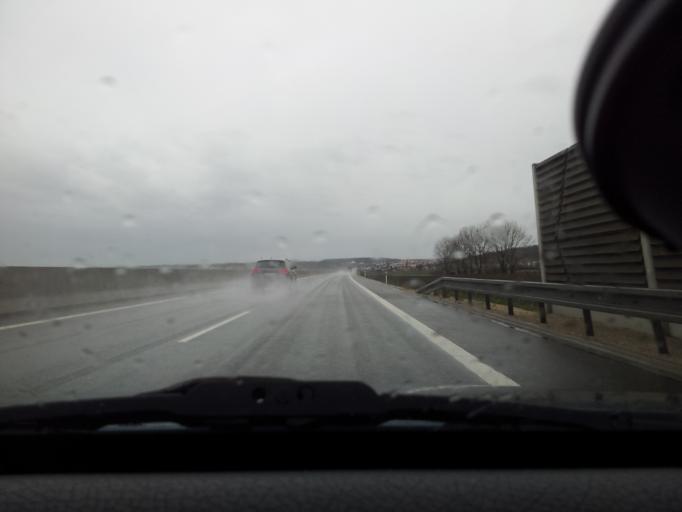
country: SK
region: Nitriansky
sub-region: Okres Nitra
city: Nitra
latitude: 48.2955
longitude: 18.1141
